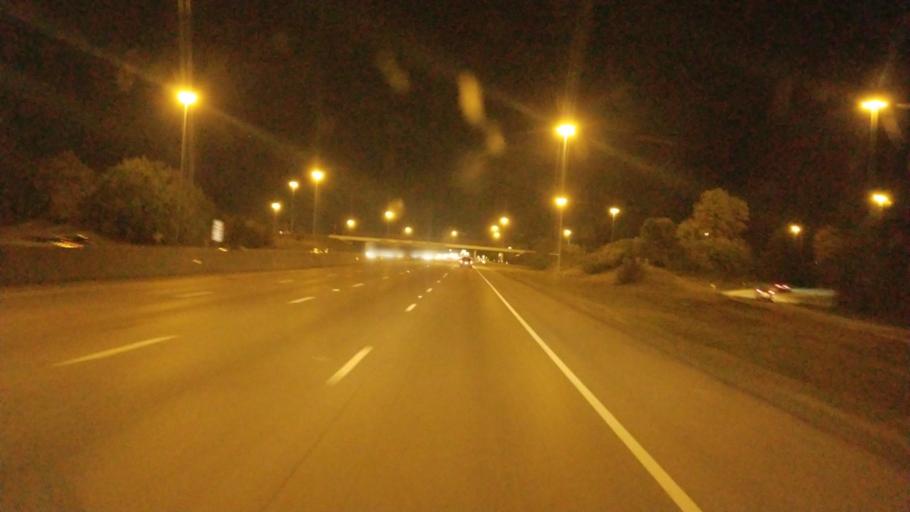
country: US
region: Ohio
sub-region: Franklin County
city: Westerville
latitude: 40.1049
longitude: -82.9451
